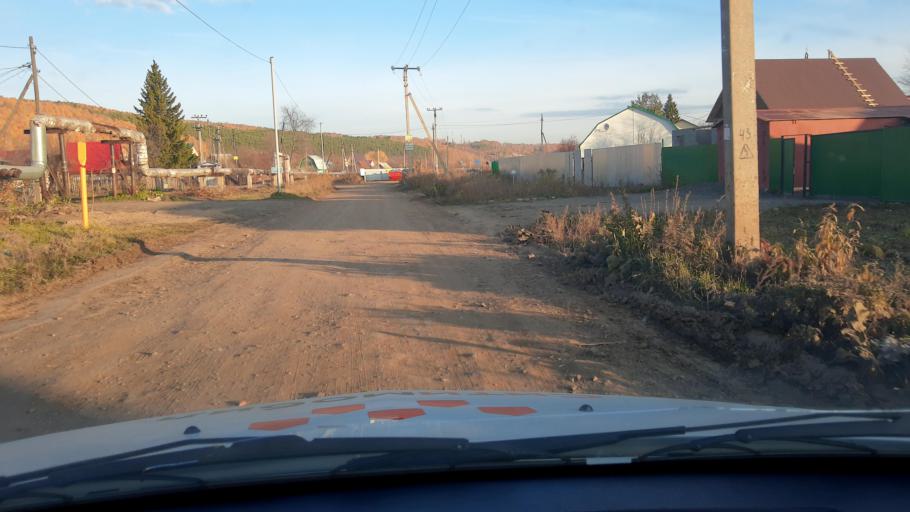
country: RU
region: Bashkortostan
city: Ufa
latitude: 54.8164
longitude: 56.1541
